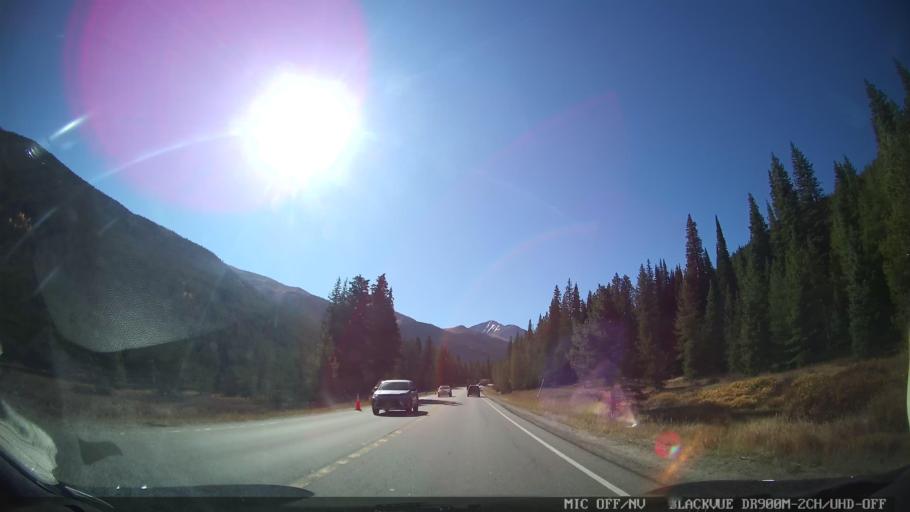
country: US
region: Colorado
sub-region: Summit County
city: Frisco
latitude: 39.4883
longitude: -106.1341
